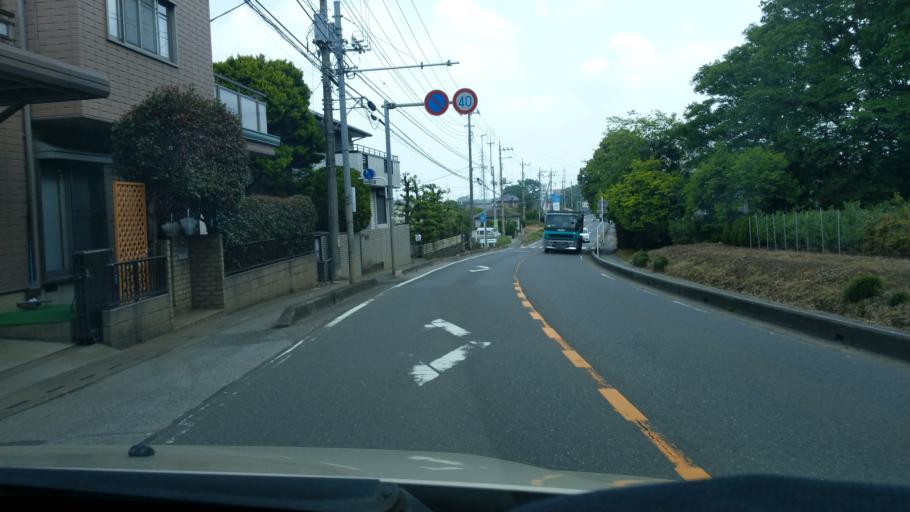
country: JP
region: Saitama
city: Iwatsuki
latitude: 35.9090
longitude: 139.7048
